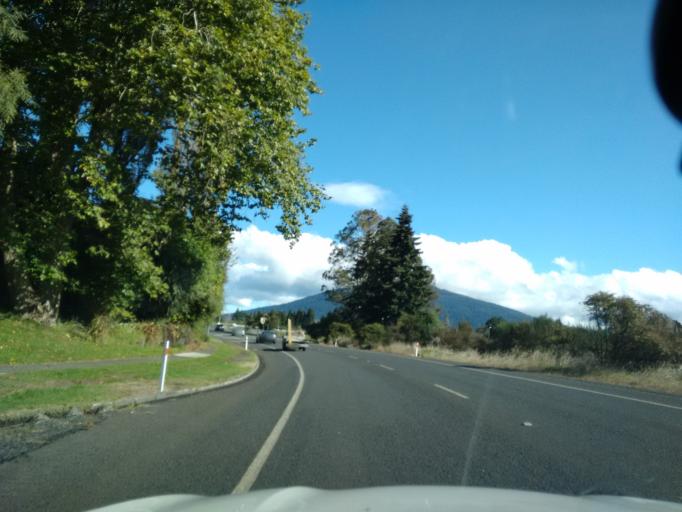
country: NZ
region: Waikato
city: Turangi
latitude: -38.9832
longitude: 175.8203
